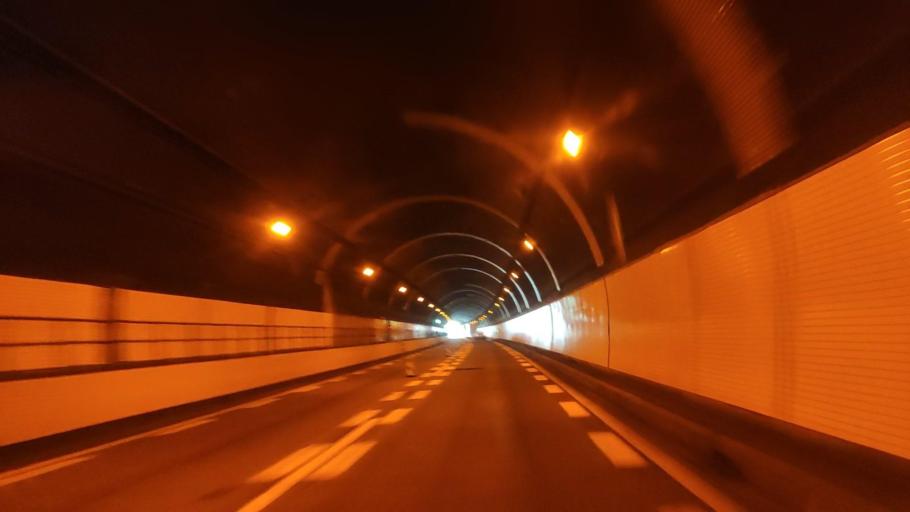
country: JP
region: Niigata
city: Joetsu
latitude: 37.1093
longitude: 138.0468
